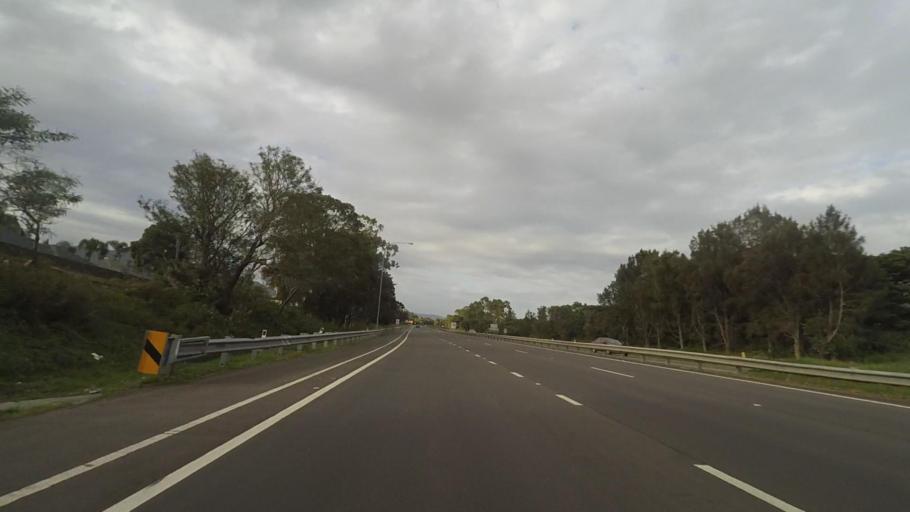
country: AU
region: New South Wales
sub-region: Wollongong
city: Fairy Meadow
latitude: -34.4046
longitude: 150.8924
